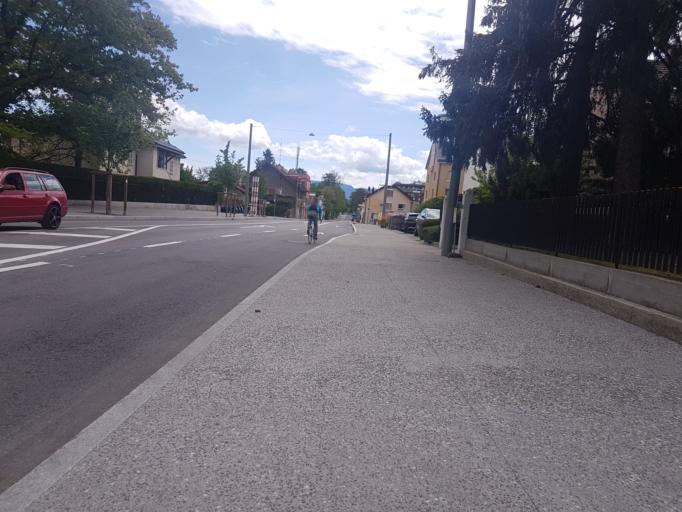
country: CH
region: Geneva
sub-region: Geneva
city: Versoix
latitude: 46.2904
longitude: 6.1657
